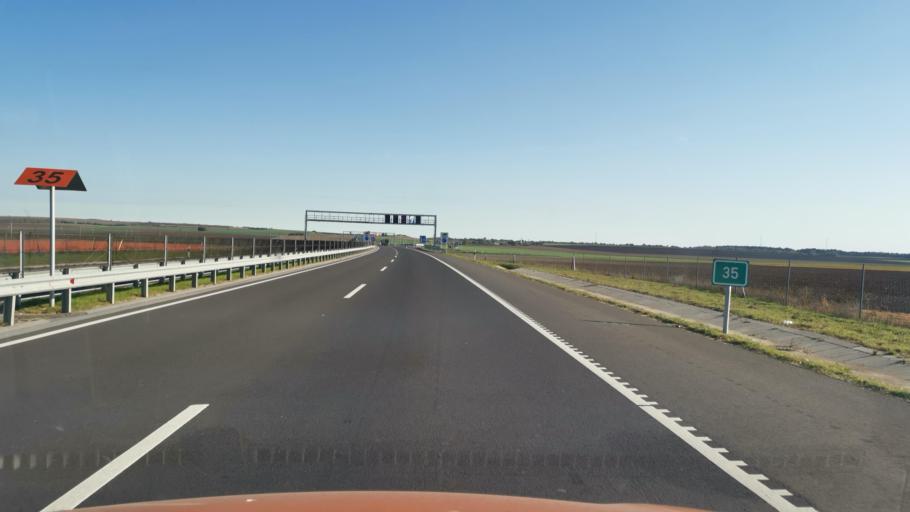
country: HU
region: Borsod-Abauj-Zemplen
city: Arnot
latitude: 48.1497
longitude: 20.8633
